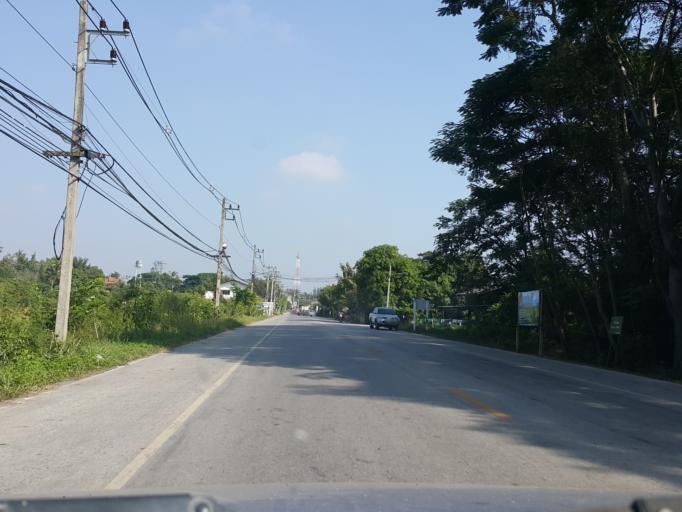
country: TH
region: Chiang Mai
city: San Kamphaeng
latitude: 18.8133
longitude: 99.1215
